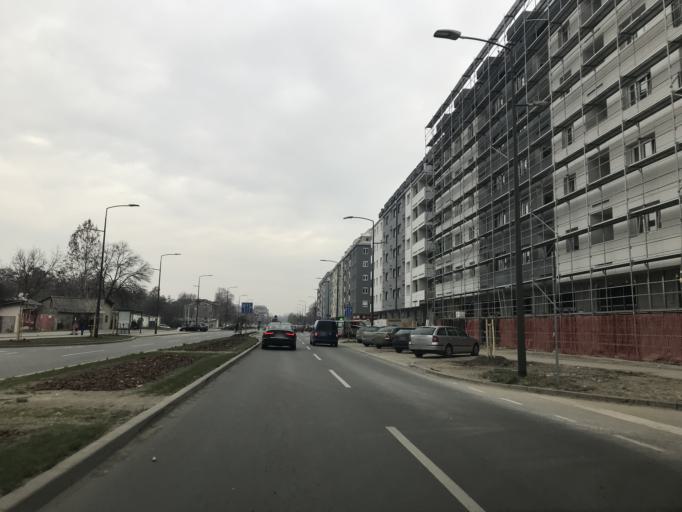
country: RS
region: Autonomna Pokrajina Vojvodina
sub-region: Juznobacki Okrug
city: Novi Sad
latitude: 45.2472
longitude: 19.7999
